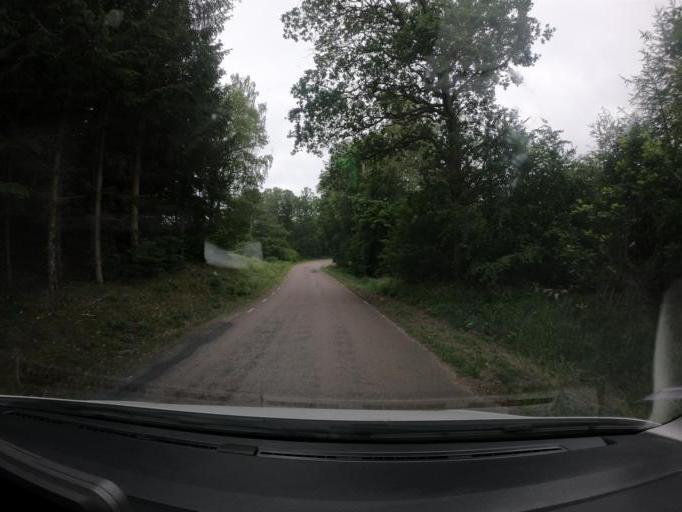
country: SE
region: Skane
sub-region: Perstorps Kommun
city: Perstorp
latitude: 56.0963
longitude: 13.3348
